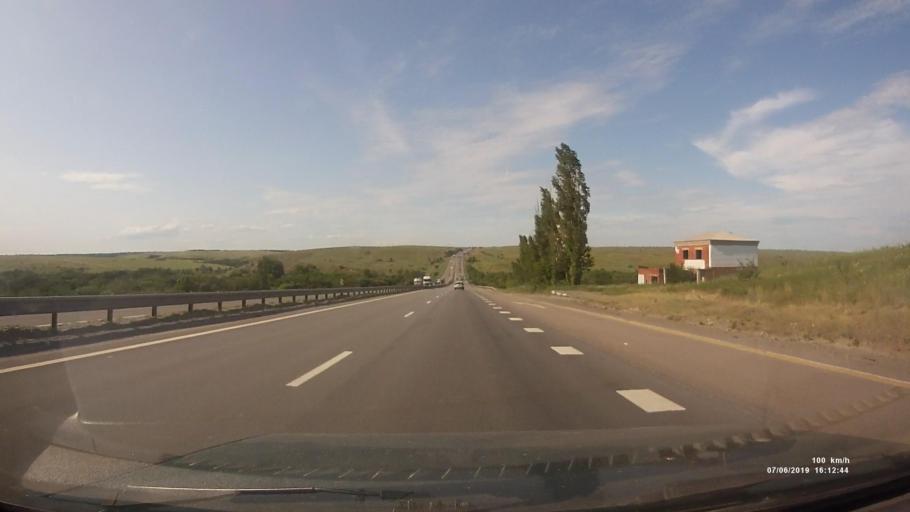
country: RU
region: Rostov
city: Likhoy
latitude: 48.1338
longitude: 40.2592
